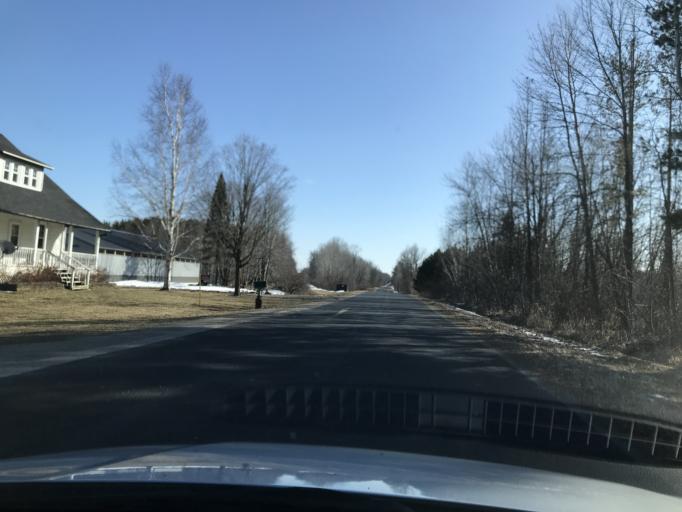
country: US
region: Wisconsin
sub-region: Marinette County
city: Peshtigo
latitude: 45.1611
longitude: -87.7596
